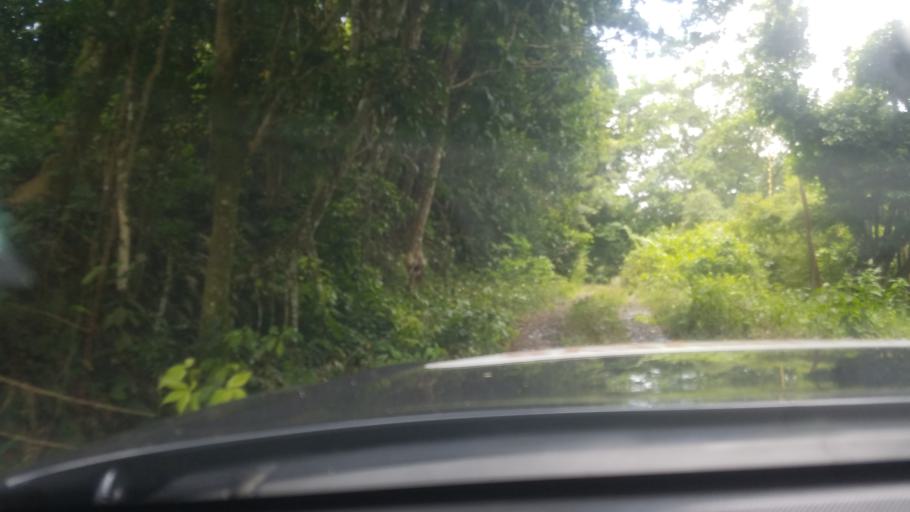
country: LC
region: Anse-la-Raye
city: Anse La Raye
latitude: 13.9109
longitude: -61.0069
